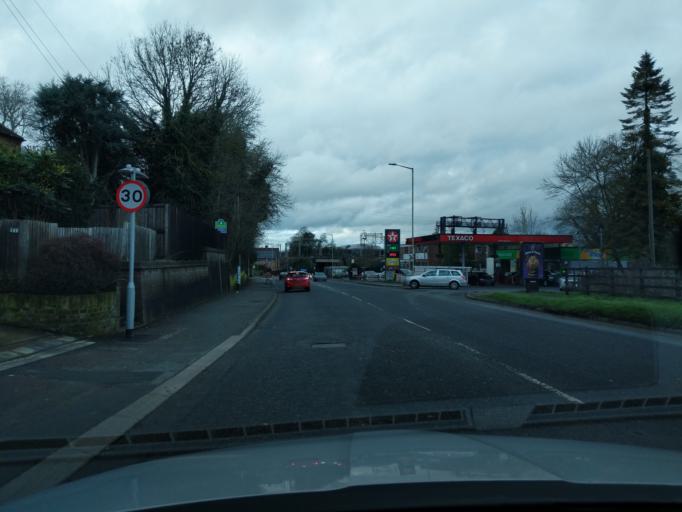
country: GB
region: England
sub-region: Hertfordshire
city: Kings Langley
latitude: 51.7253
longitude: -0.4530
